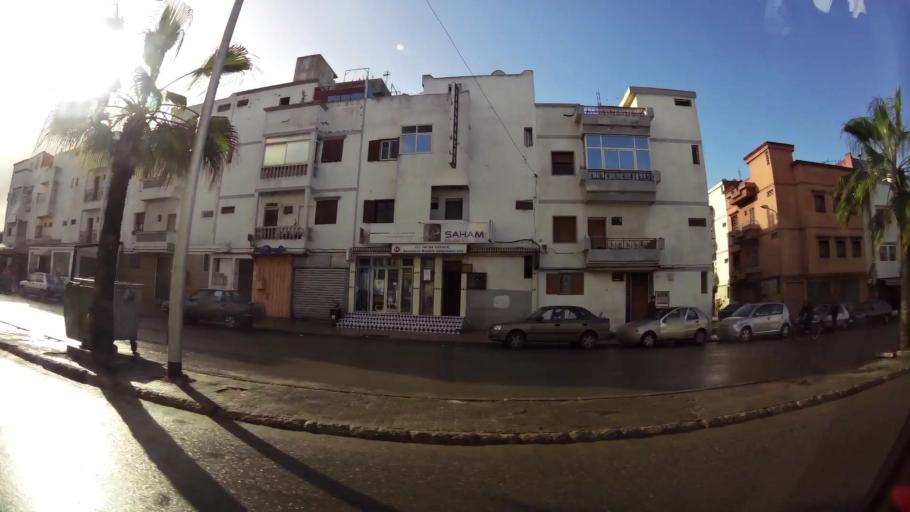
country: MA
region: Grand Casablanca
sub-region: Casablanca
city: Casablanca
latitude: 33.5540
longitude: -7.6878
